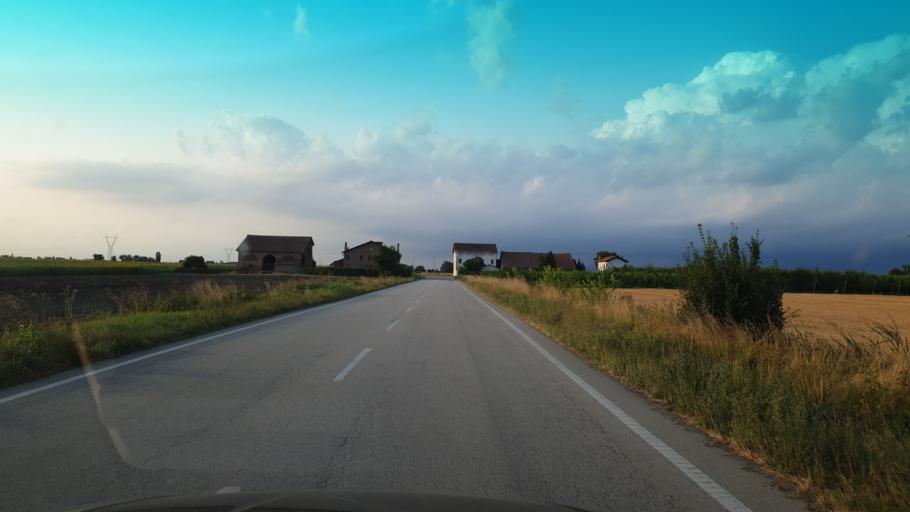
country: IT
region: Veneto
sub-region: Provincia di Rovigo
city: San Bellino
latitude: 45.0568
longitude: 11.5822
